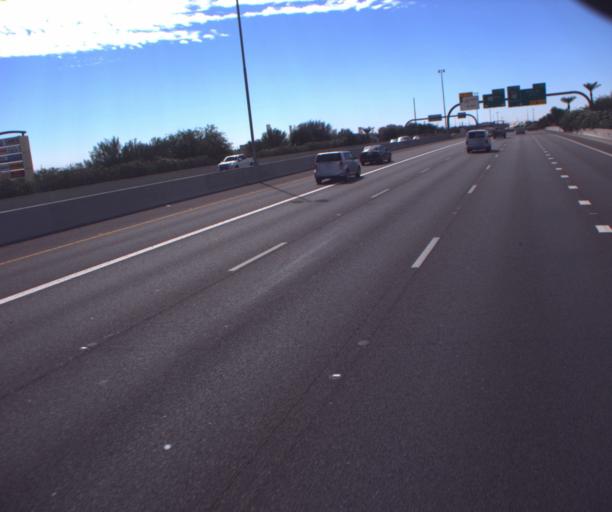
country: US
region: Arizona
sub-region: Maricopa County
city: Chandler
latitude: 33.3076
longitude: -111.8945
